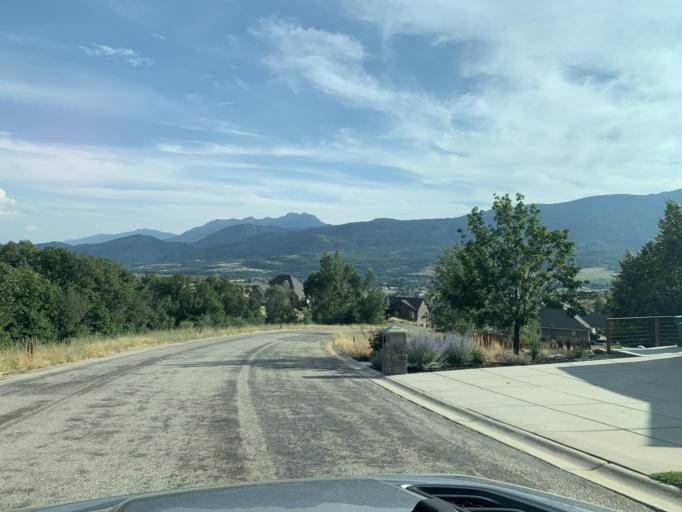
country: US
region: Utah
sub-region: Weber County
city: Wolf Creek
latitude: 41.3247
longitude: -111.8153
